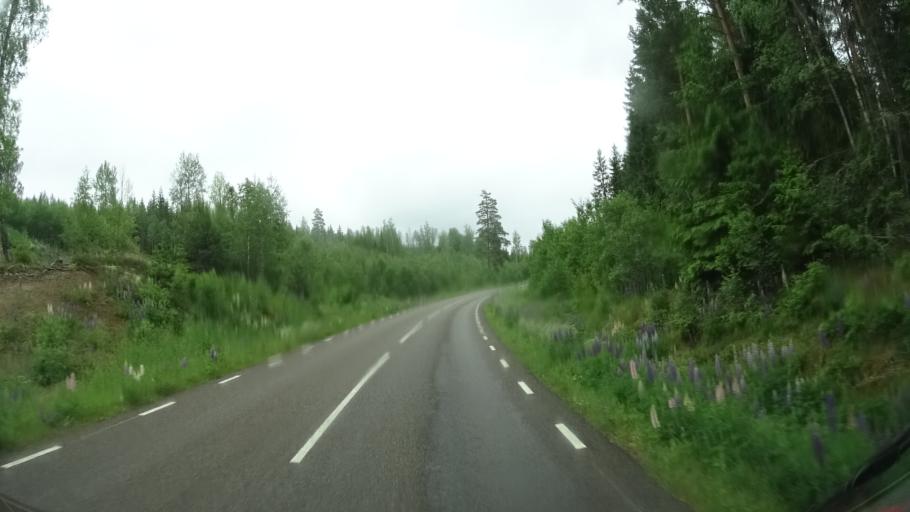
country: SE
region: Joenkoeping
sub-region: Eksjo Kommun
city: Mariannelund
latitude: 57.6646
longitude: 15.6001
